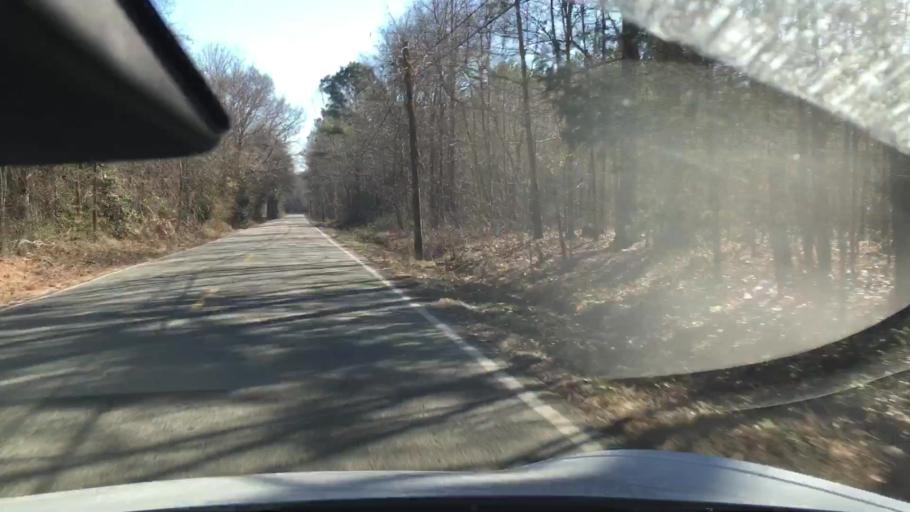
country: US
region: Virginia
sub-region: Henrico County
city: Short Pump
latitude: 37.5813
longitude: -77.7411
